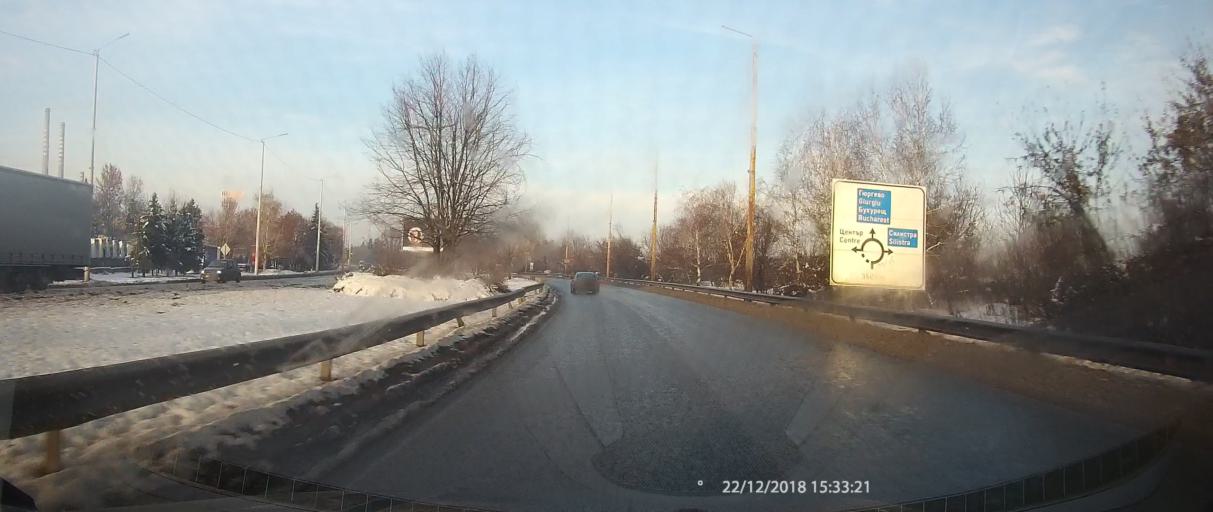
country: BG
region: Ruse
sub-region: Obshtina Ruse
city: Ruse
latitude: 43.8573
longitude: 26.0140
